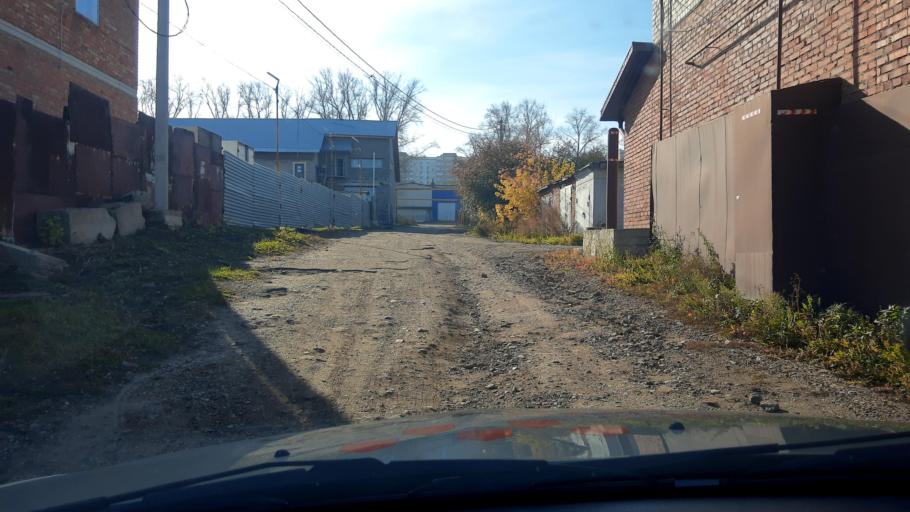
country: RU
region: Bashkortostan
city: Ufa
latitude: 54.8286
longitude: 56.0732
